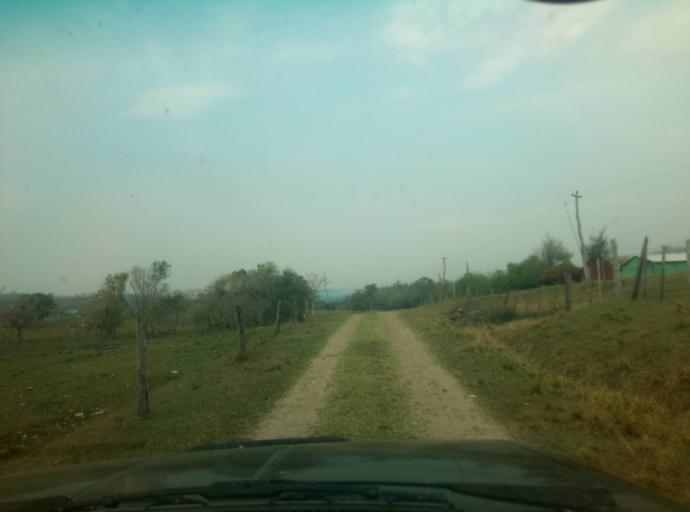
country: PY
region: Caaguazu
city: San Joaquin
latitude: -25.1044
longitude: -56.1277
